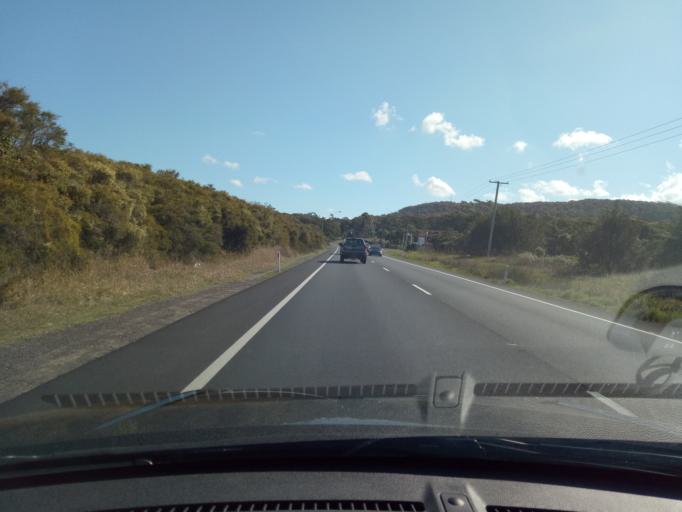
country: AU
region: New South Wales
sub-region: Gosford Shire
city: Forresters Beach
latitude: -33.4121
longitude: 151.4558
